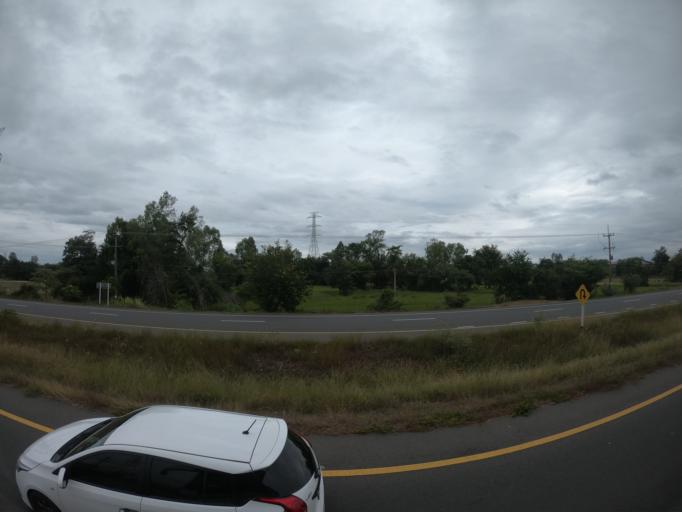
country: TH
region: Kalasin
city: Khong Chai
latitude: 16.1288
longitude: 103.4677
